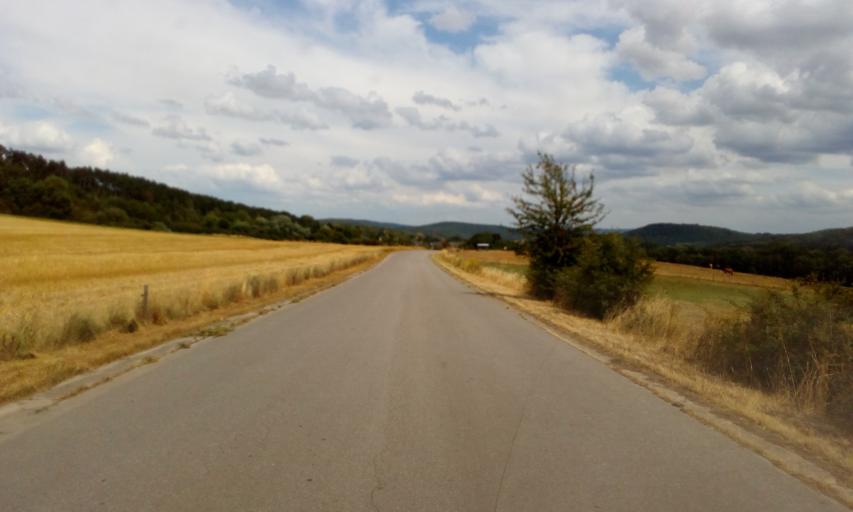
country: BE
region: Wallonia
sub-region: Province du Luxembourg
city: Wellin
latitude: 50.1064
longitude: 5.1275
